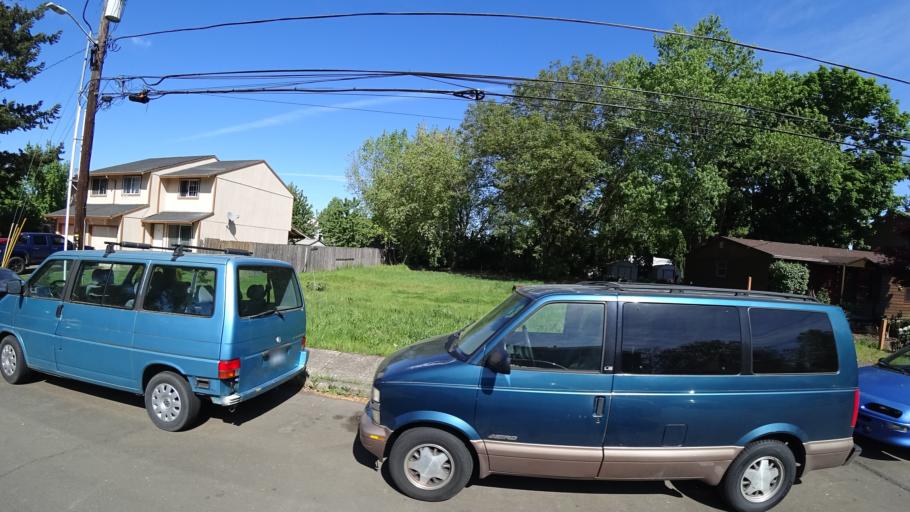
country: US
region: Oregon
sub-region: Washington County
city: Hillsboro
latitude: 45.5145
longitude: -122.9677
